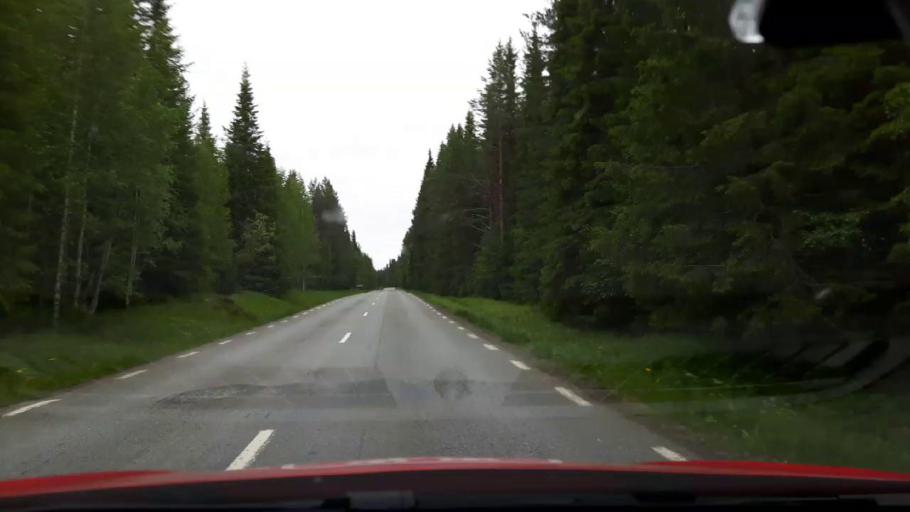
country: SE
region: Jaemtland
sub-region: Stroemsunds Kommun
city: Stroemsund
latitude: 63.4646
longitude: 15.4559
